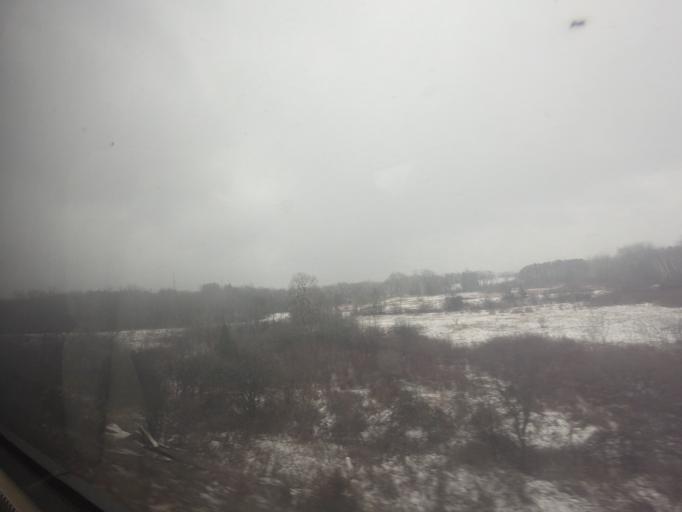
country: CA
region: Ontario
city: Cobourg
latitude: 43.9262
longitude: -78.4213
